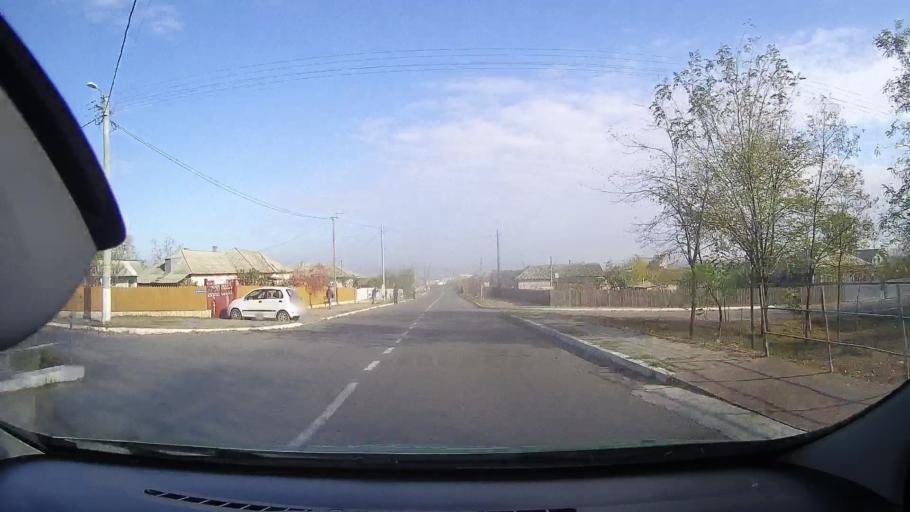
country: RO
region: Tulcea
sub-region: Comuna Mahmudia
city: Mahmudia
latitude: 45.0826
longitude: 29.0822
